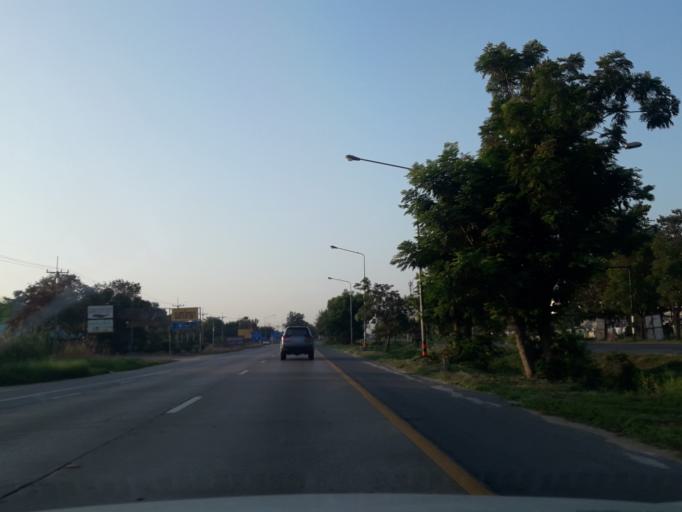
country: TH
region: Phra Nakhon Si Ayutthaya
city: Phra Nakhon Si Ayutthaya
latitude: 14.3210
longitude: 100.5277
